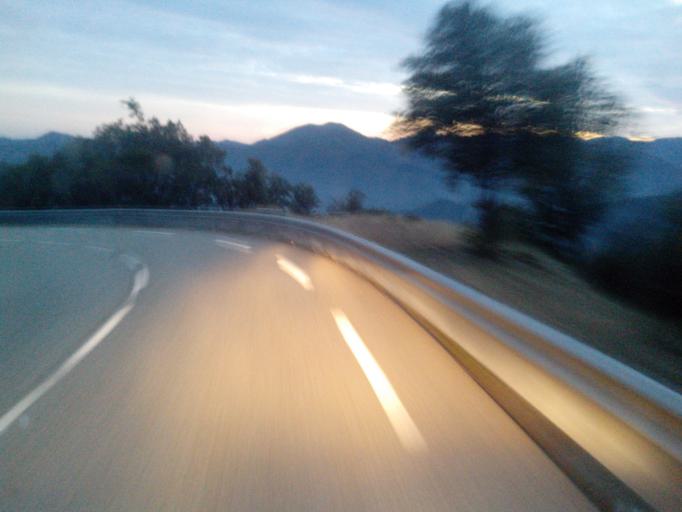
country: FR
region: Languedoc-Roussillon
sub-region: Departement du Gard
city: Saint-Jean-du-Gard
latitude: 44.1338
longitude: 3.8468
